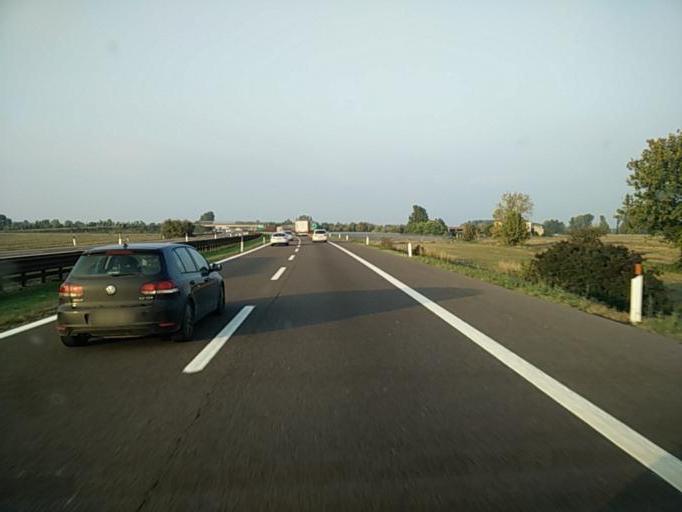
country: IT
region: Veneto
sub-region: Provincia di Verona
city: Vigasio
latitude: 45.3265
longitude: 10.9166
